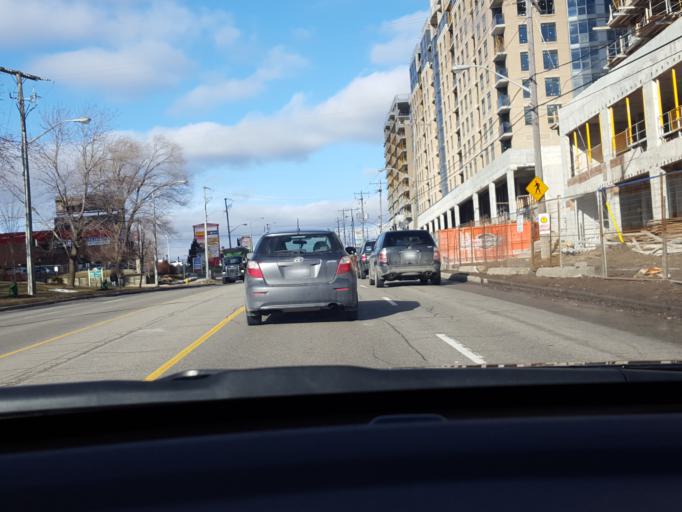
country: CA
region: Ontario
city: Concord
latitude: 43.7486
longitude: -79.5416
